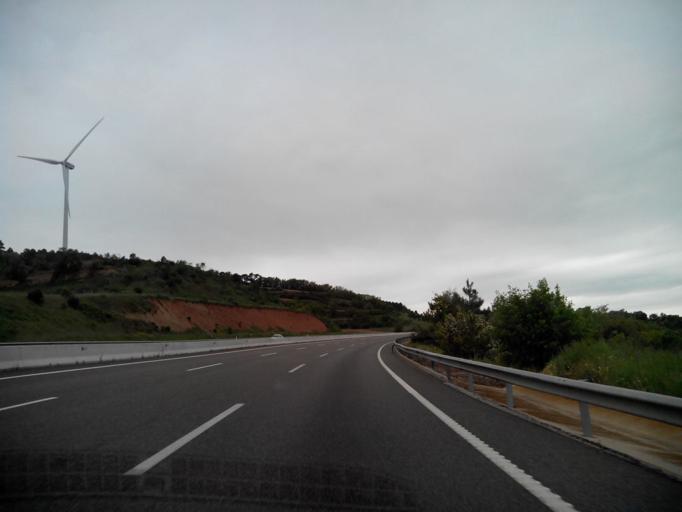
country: ES
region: Catalonia
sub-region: Provincia de Barcelona
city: Castellfollit de Riubregos
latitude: 41.7356
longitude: 1.4532
